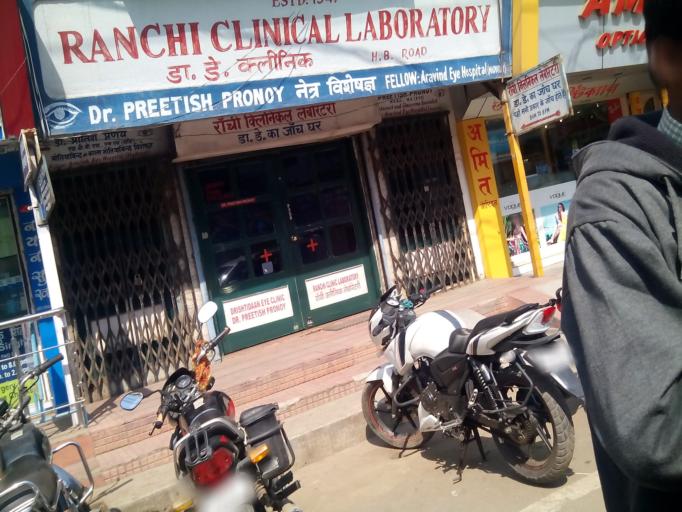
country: IN
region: Jharkhand
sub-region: Ranchi
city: Ranchi
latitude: 23.3705
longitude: 85.3261
